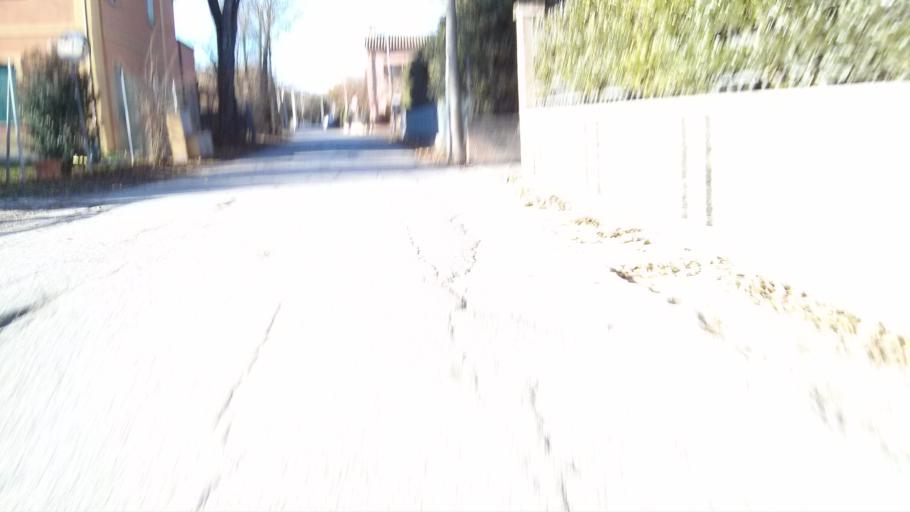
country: IT
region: The Marches
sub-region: Provincia di Pesaro e Urbino
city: Fano
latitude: 43.8471
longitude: 13.0052
